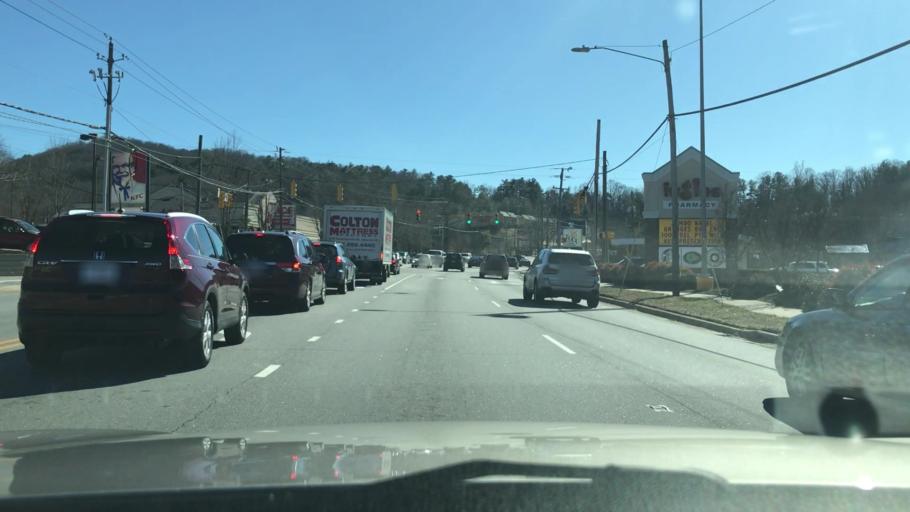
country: US
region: North Carolina
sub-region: Buncombe County
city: Royal Pines
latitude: 35.5003
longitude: -82.5221
